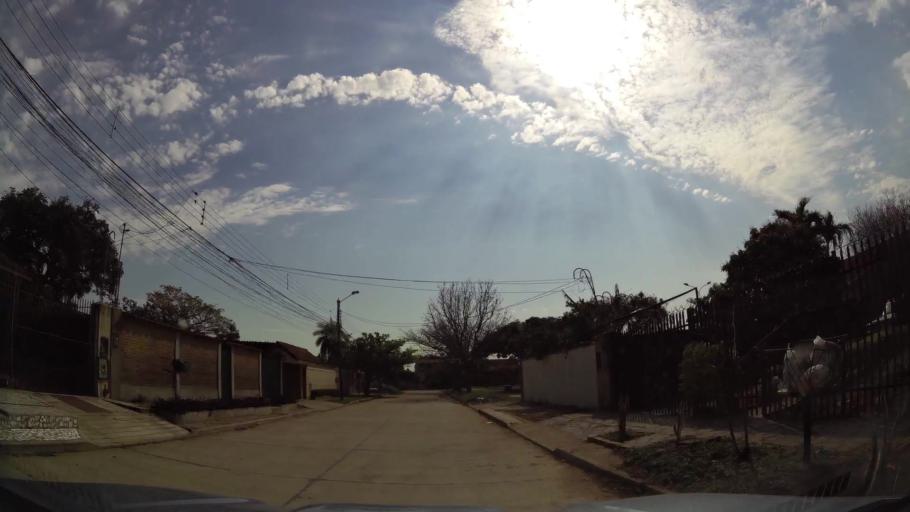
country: BO
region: Santa Cruz
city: Santa Cruz de la Sierra
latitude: -17.7279
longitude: -63.1550
